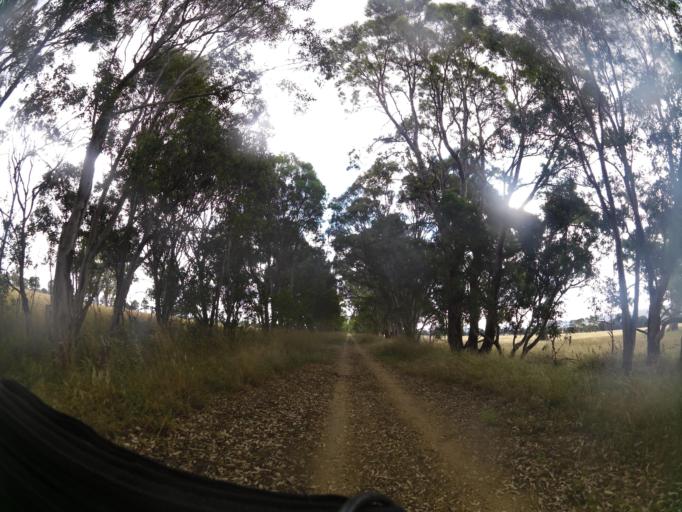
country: AU
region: Victoria
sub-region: Wellington
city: Heyfield
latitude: -38.0292
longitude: 146.6648
